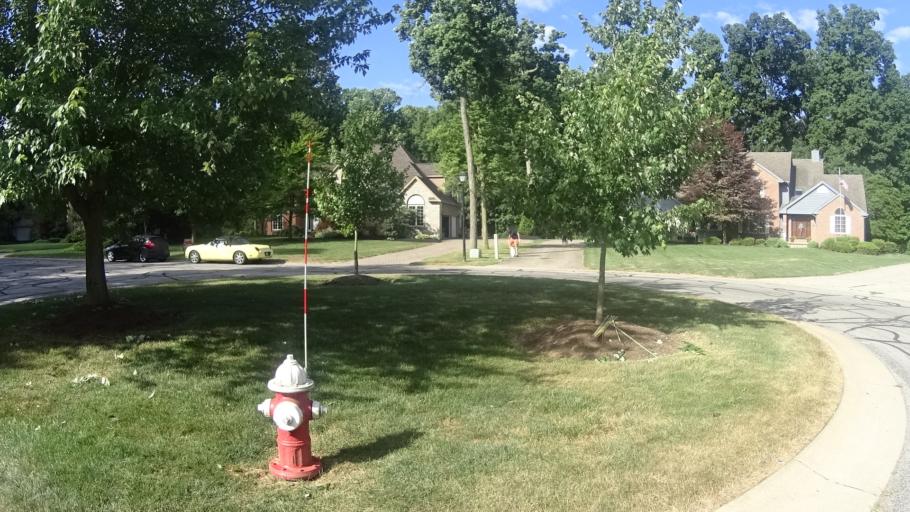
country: US
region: Ohio
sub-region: Erie County
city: Sandusky
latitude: 41.4185
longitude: -82.6603
